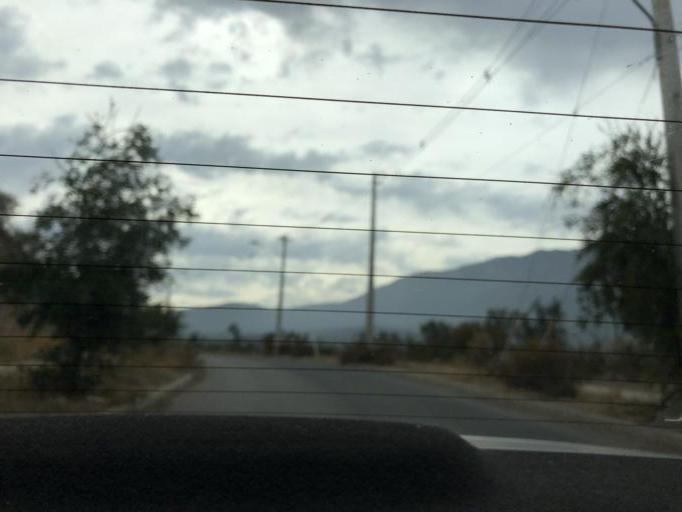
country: CL
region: Santiago Metropolitan
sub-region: Provincia de Cordillera
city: Puente Alto
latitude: -33.5920
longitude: -70.5196
